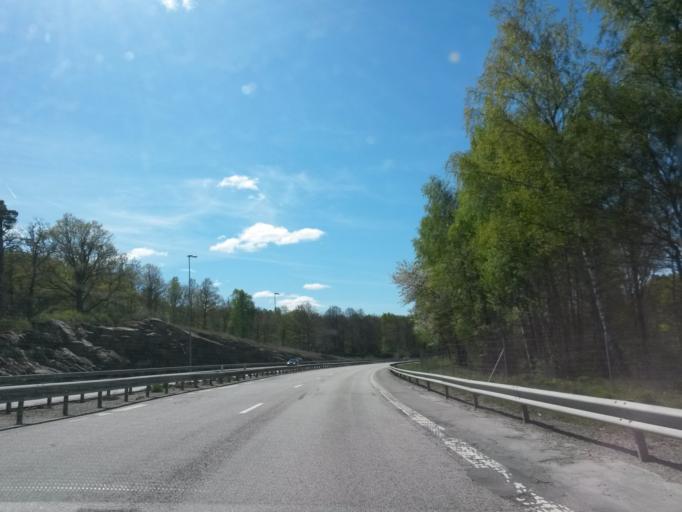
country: SE
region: Vaestra Goetaland
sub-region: Alingsas Kommun
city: Alingsas
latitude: 57.9052
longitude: 12.5014
